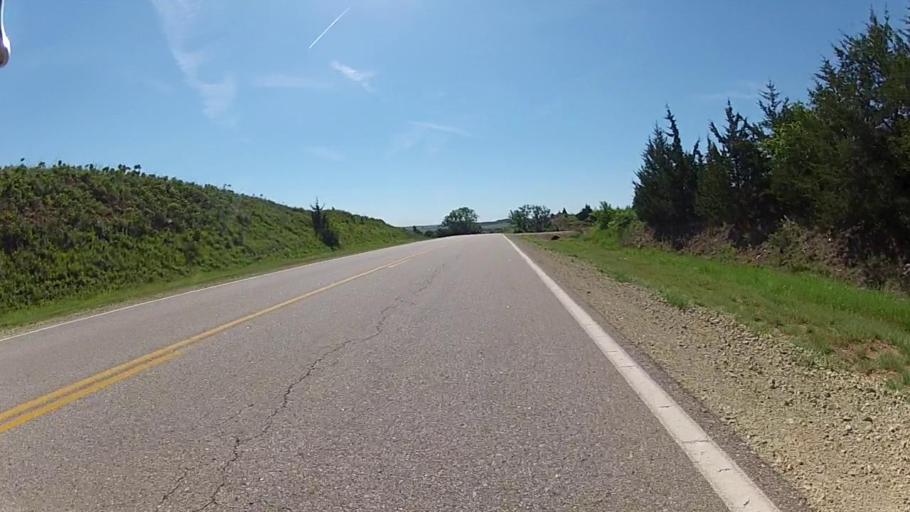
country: US
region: Kansas
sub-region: Barber County
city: Medicine Lodge
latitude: 37.2781
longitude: -98.7391
